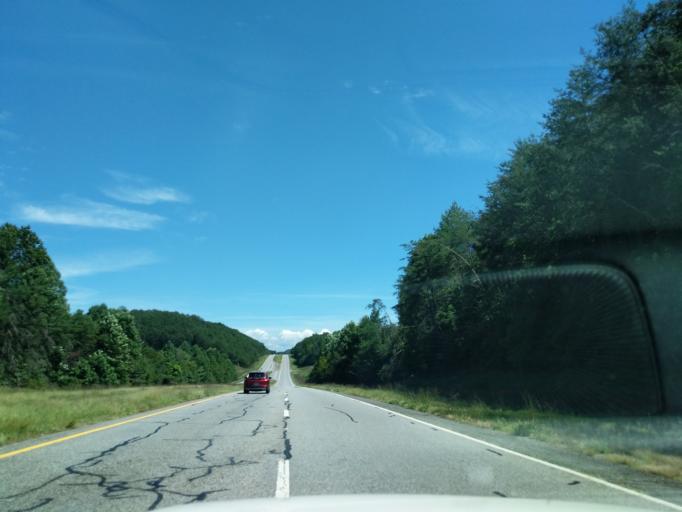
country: US
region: Georgia
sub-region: Fannin County
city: Blue Ridge
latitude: 34.8916
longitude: -84.2415
